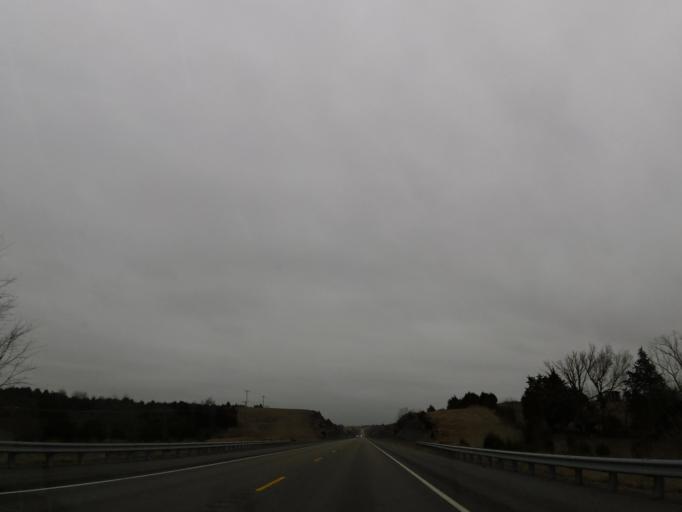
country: US
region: Kentucky
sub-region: Lincoln County
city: Stanford
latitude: 37.5120
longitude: -84.5961
